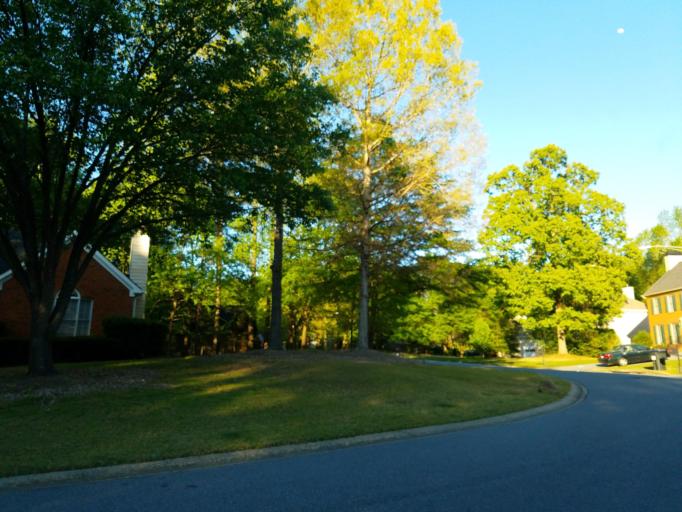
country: US
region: Georgia
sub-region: Cobb County
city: Powder Springs
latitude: 33.9231
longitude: -84.6396
